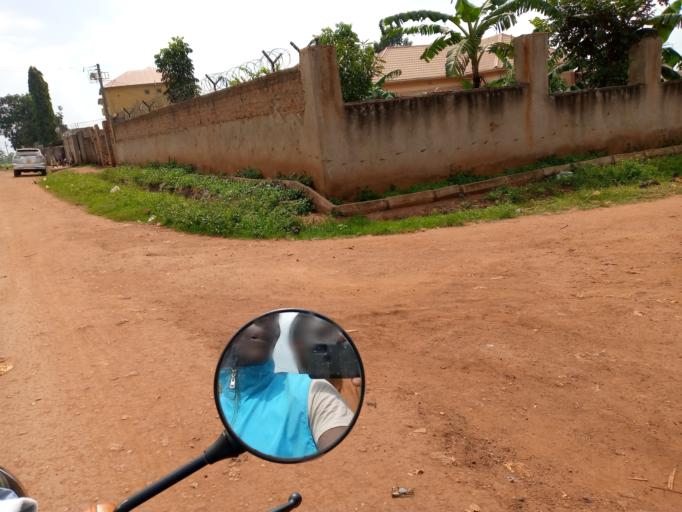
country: UG
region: Eastern Region
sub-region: Mbale District
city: Mbale
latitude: 1.0835
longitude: 34.1593
